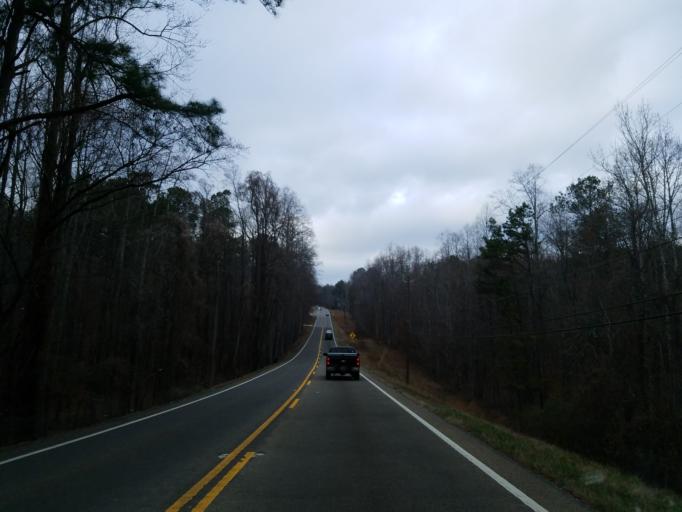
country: US
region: Georgia
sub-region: Cherokee County
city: Canton
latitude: 34.2832
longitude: -84.5120
